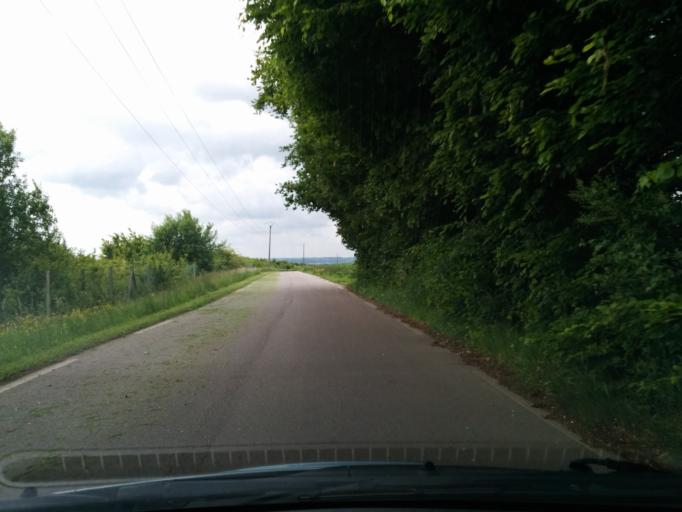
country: FR
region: Ile-de-France
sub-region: Departement des Yvelines
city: Issou
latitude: 49.0182
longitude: 1.7921
